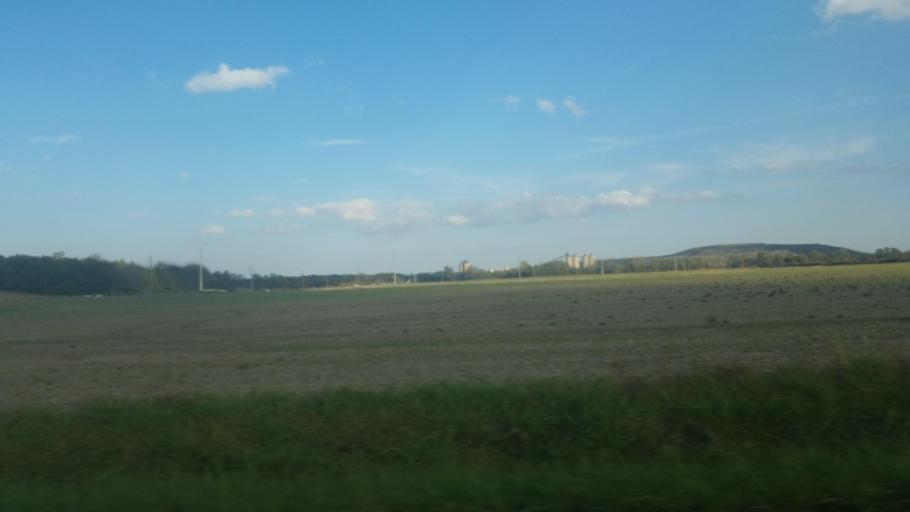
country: US
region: Illinois
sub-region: Saline County
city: Harrisburg
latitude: 37.8260
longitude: -88.6147
